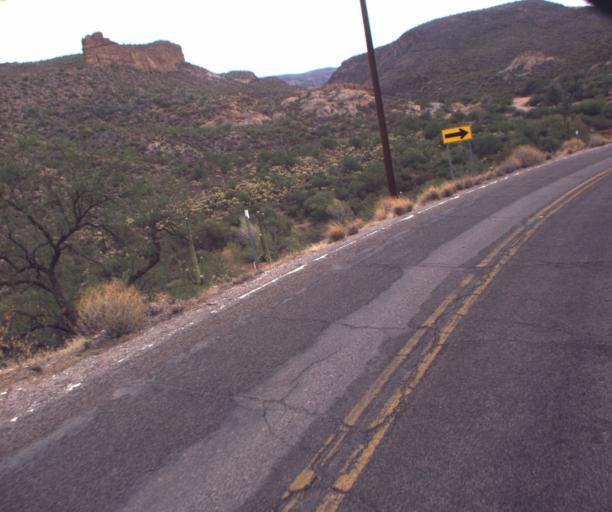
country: US
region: Arizona
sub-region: Pinal County
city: Apache Junction
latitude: 33.5263
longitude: -111.3934
